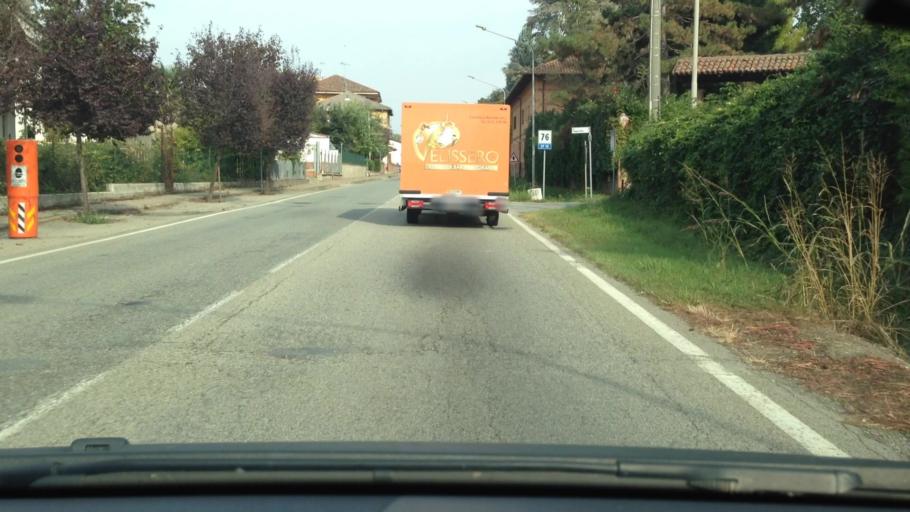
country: IT
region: Piedmont
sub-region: Provincia di Alessandria
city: Quattordio
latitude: 44.8974
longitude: 8.4033
